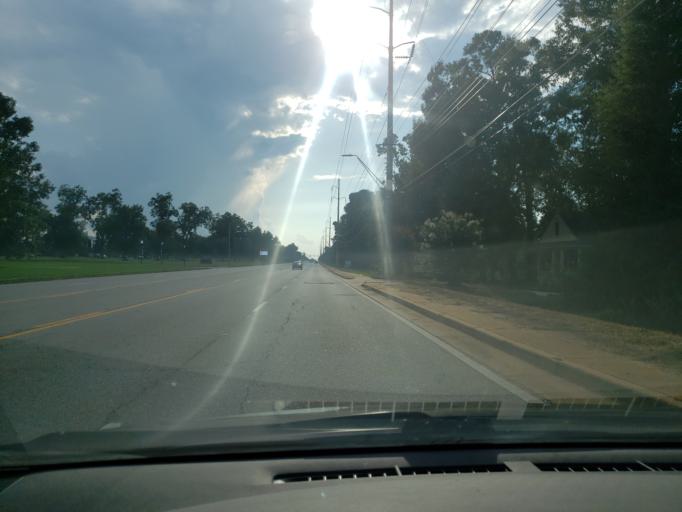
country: US
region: Georgia
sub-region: Dougherty County
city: Albany
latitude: 31.5859
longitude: -84.2092
